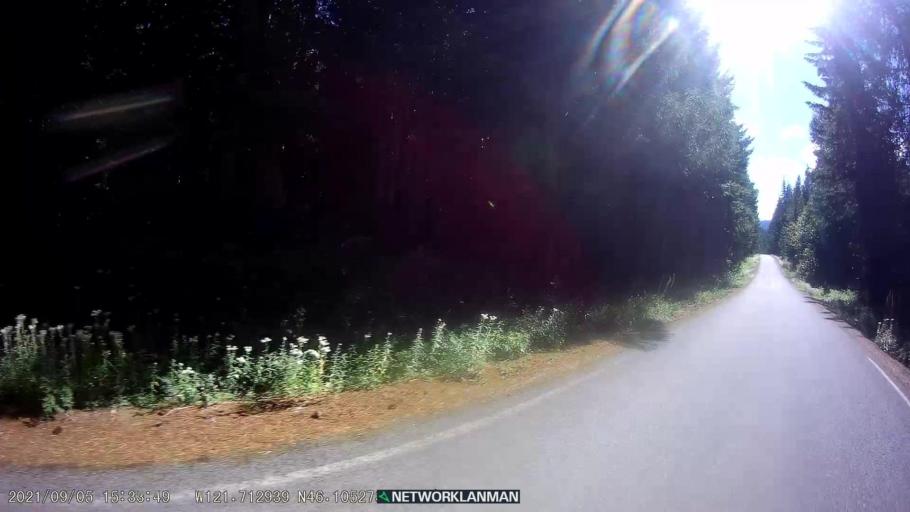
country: US
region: Washington
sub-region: Skamania County
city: Carson
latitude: 46.1051
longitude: -121.7133
